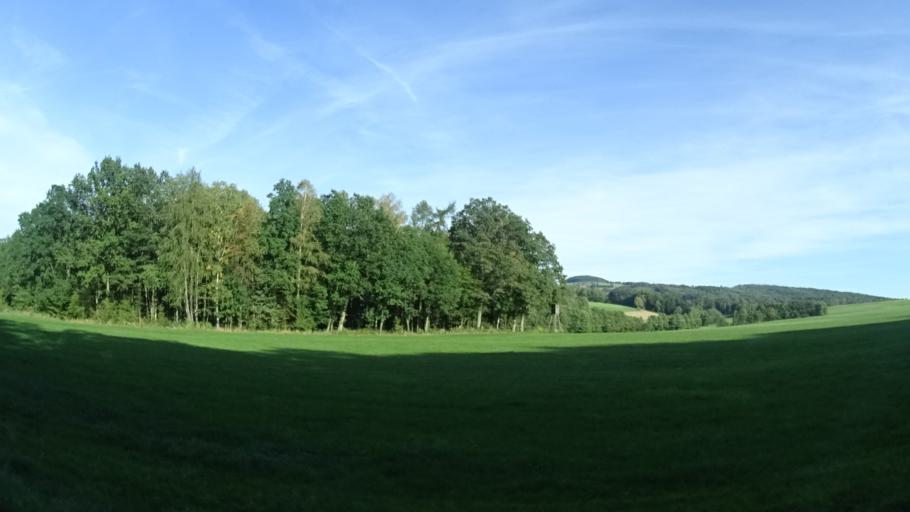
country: DE
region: Hesse
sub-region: Regierungsbezirk Kassel
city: Dipperz
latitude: 50.5402
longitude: 9.8329
